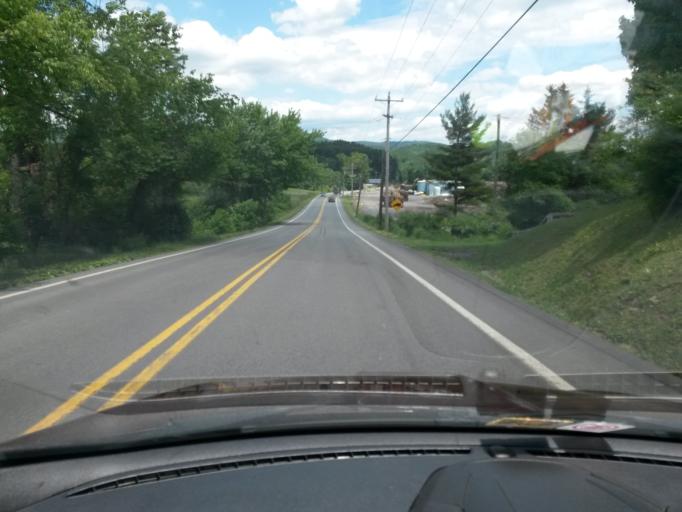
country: US
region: West Virginia
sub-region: Greenbrier County
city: Rainelle
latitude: 37.9531
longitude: -80.6654
